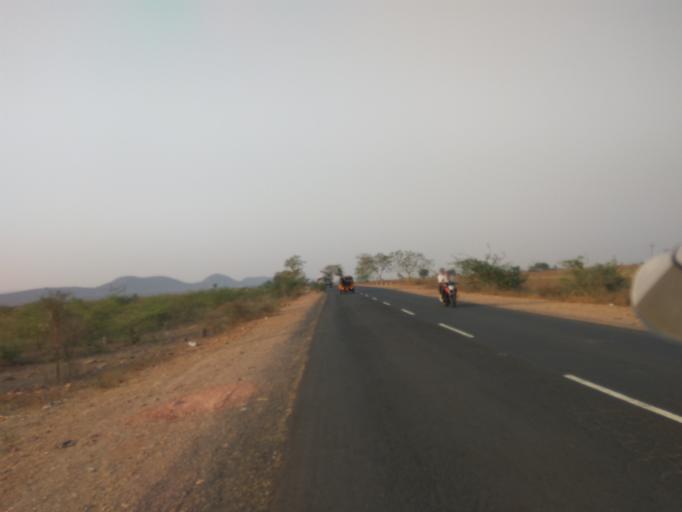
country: IN
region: Andhra Pradesh
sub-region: Prakasam
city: Cumbum
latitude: 15.6221
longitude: 79.1341
